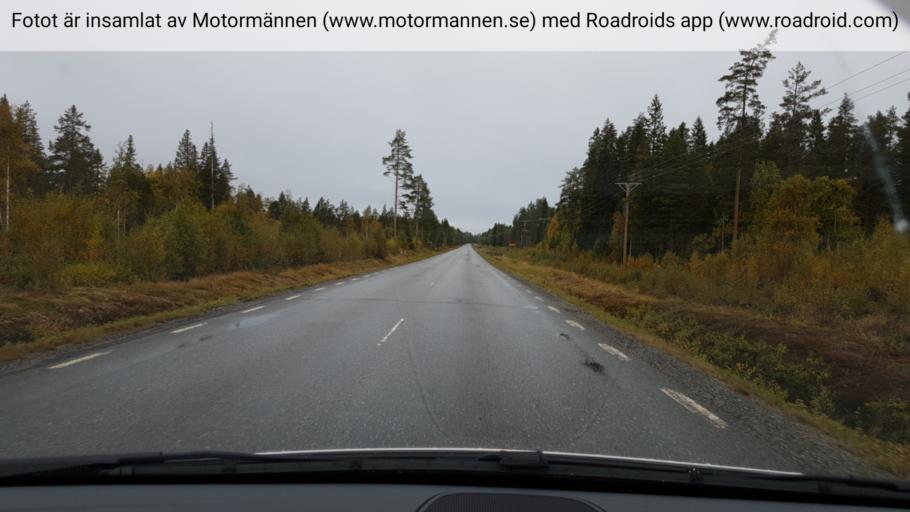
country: SE
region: Vaesterbotten
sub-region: Umea Kommun
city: Ersmark
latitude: 64.0599
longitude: 20.2216
